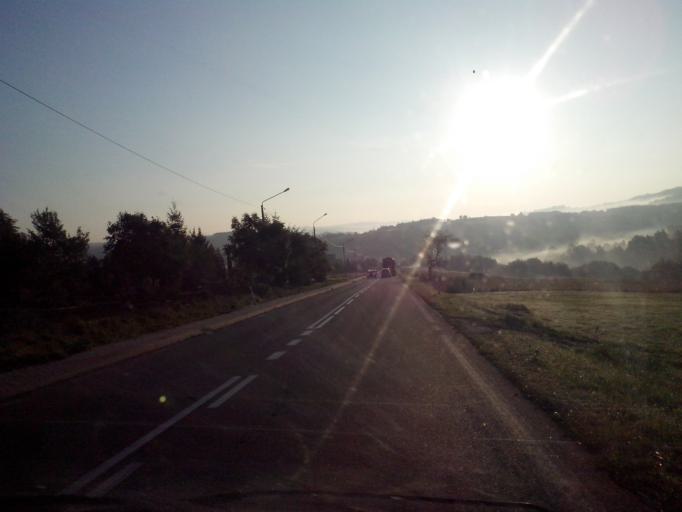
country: PL
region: Subcarpathian Voivodeship
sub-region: Powiat brzozowski
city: Golcowa
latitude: 49.8097
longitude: 22.0337
